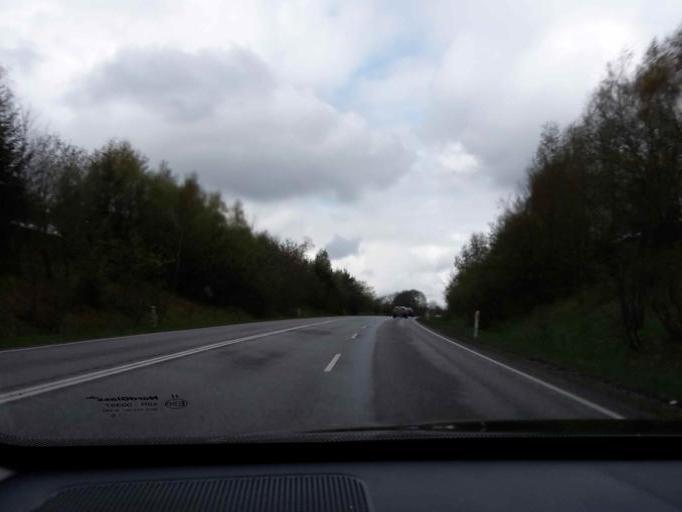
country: DK
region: South Denmark
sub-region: Vejle Kommune
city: Jelling
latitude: 55.6947
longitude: 9.3905
